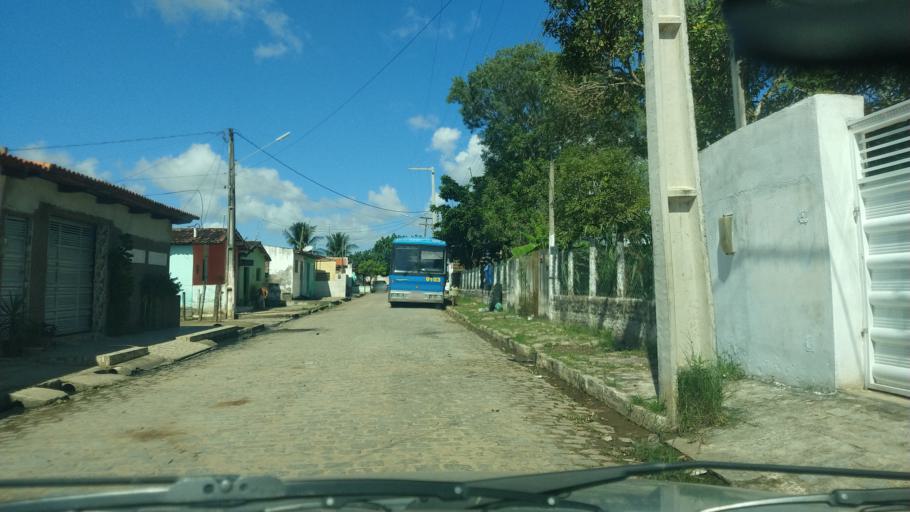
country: BR
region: Rio Grande do Norte
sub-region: Sao Goncalo Do Amarante
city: Sao Goncalo do Amarante
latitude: -5.8212
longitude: -35.3142
